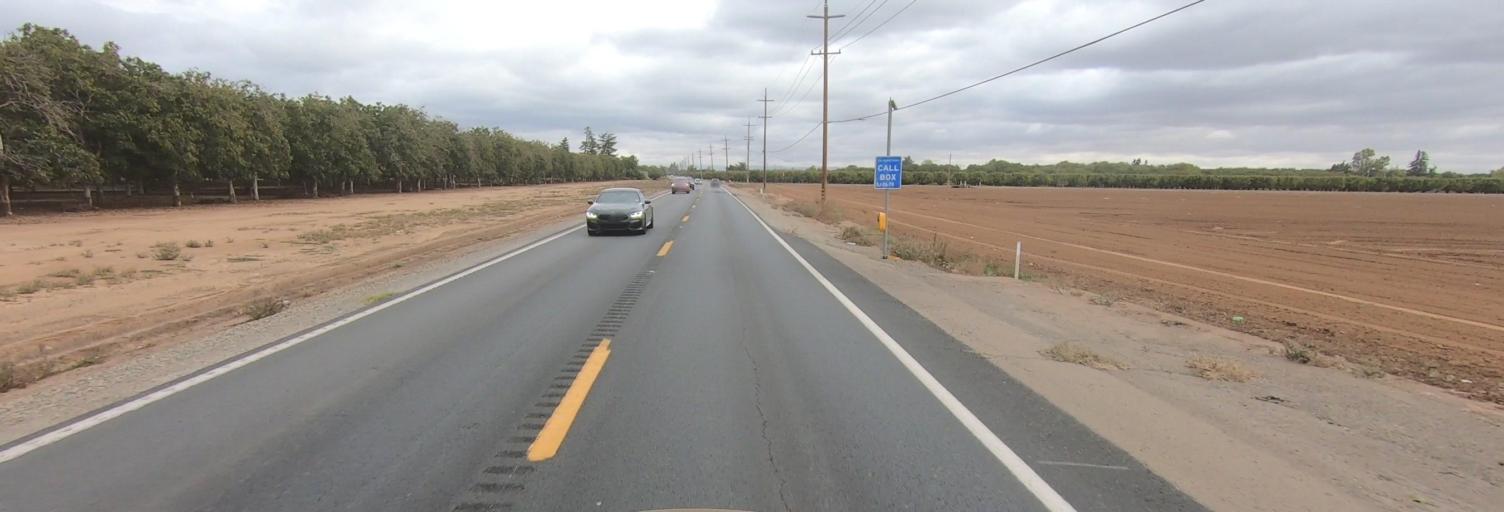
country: US
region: California
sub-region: San Joaquin County
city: Linden
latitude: 38.0062
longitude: -121.1304
